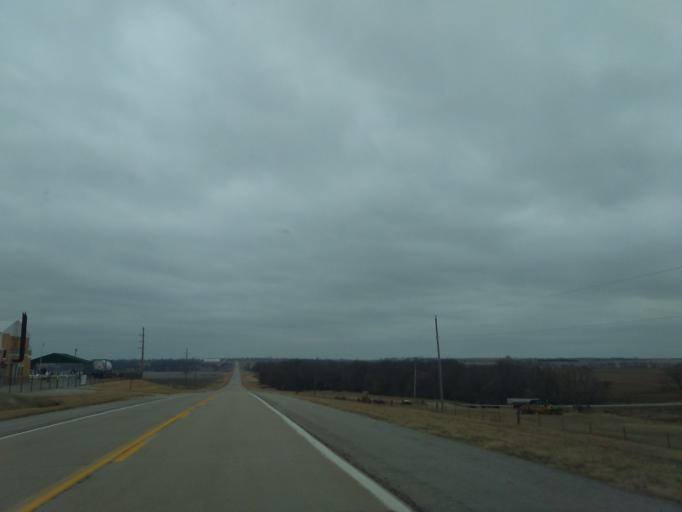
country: US
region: Nebraska
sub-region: Richardson County
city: Falls City
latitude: 40.1183
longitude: -95.6057
